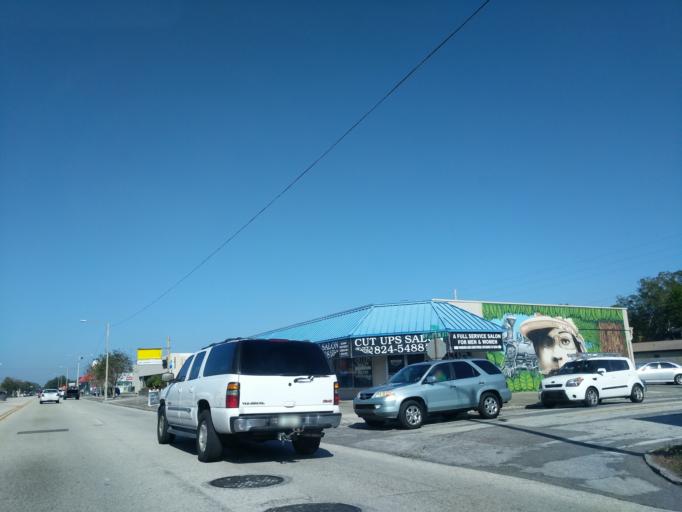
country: US
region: Florida
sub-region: Pinellas County
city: Saint Petersburg
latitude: 27.7957
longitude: -82.6467
